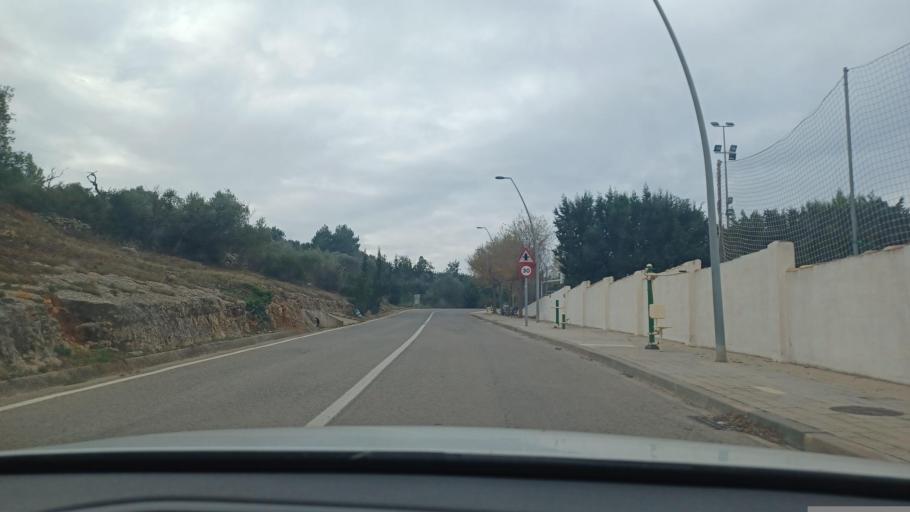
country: ES
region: Catalonia
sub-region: Provincia de Tarragona
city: Ulldecona
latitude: 40.6527
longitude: 0.4689
